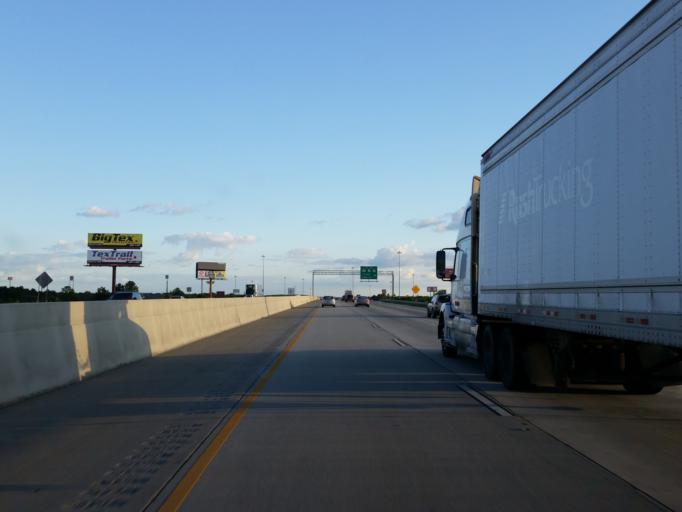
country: US
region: Georgia
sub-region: Crisp County
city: Cordele
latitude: 31.9658
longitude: -83.7525
